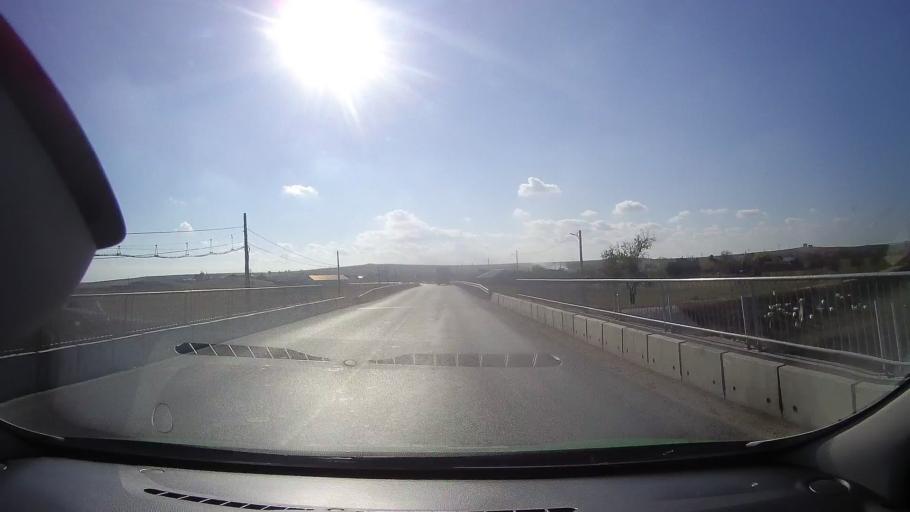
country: RO
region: Tulcea
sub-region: Comuna Baia
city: Baia
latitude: 44.7238
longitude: 28.6798
